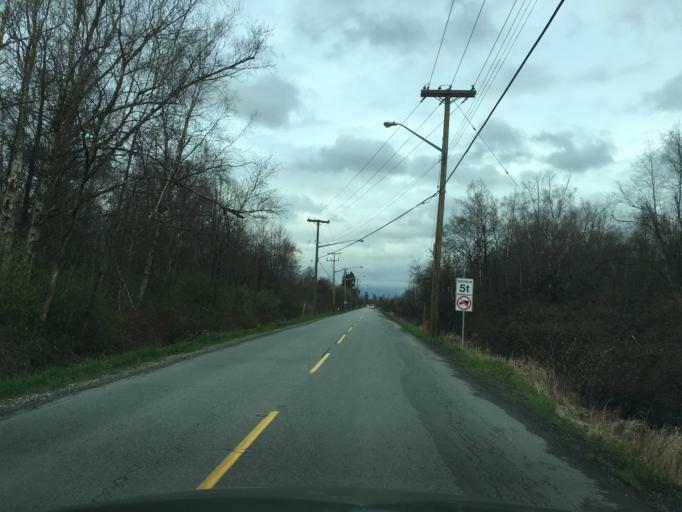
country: CA
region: British Columbia
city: Ladner
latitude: 49.1556
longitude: -123.0690
